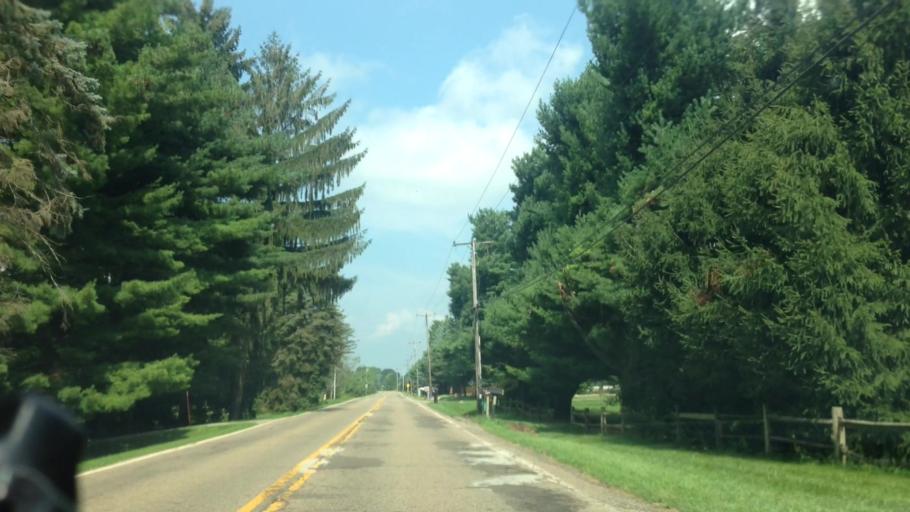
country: US
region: Ohio
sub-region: Stark County
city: Canal Fulton
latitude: 40.8390
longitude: -81.5740
